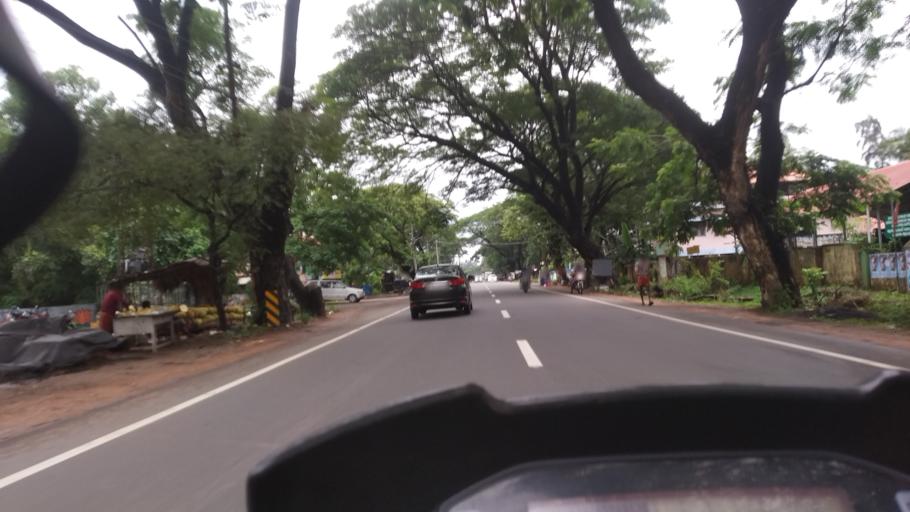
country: IN
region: Kerala
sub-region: Alappuzha
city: Alleppey
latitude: 9.4629
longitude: 76.3397
